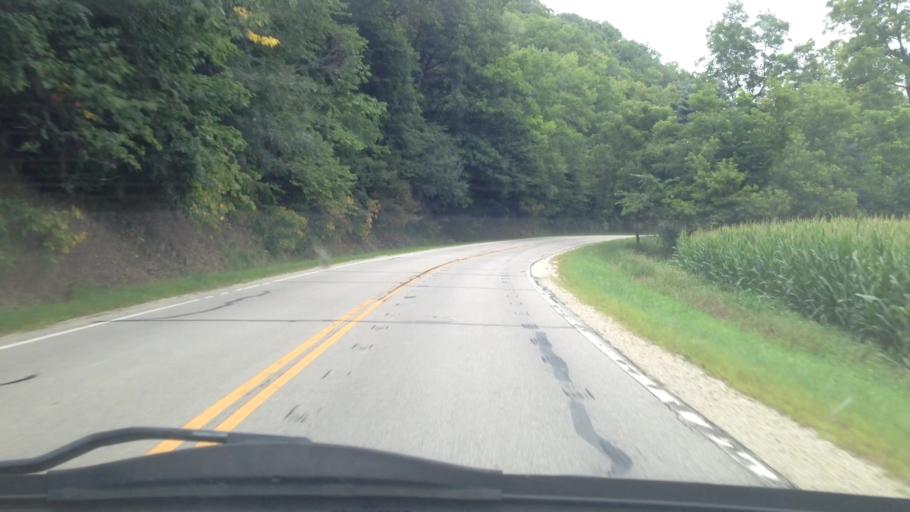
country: US
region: Minnesota
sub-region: Fillmore County
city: Preston
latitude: 43.7307
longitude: -91.9654
